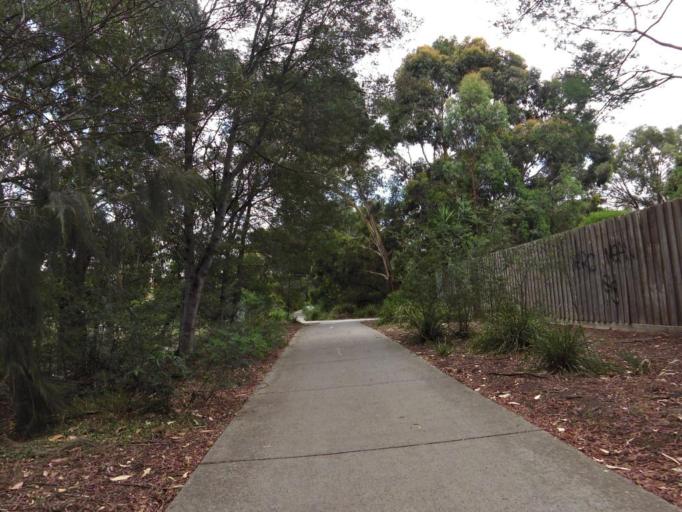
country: AU
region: Victoria
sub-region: Monash
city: Ashwood
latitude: -37.8654
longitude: 145.1008
